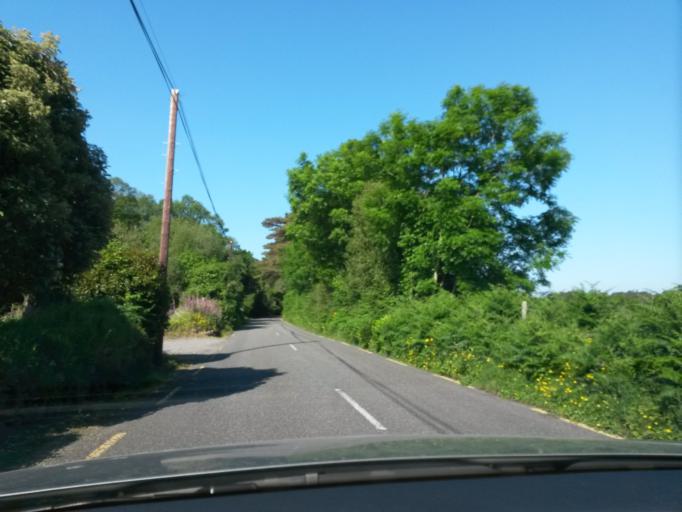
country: IE
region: Munster
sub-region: Ciarrai
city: Kenmare
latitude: 51.7620
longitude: -9.7913
